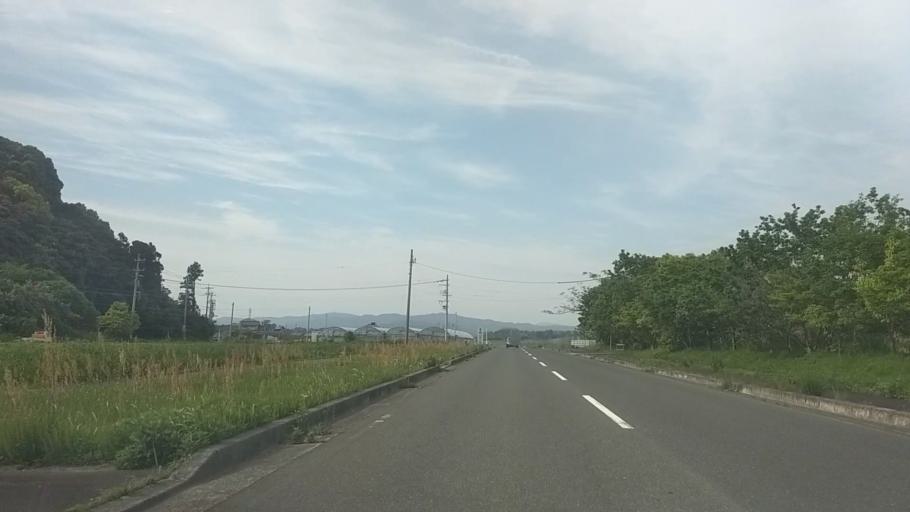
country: JP
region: Shizuoka
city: Kosai-shi
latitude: 34.7291
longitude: 137.6062
